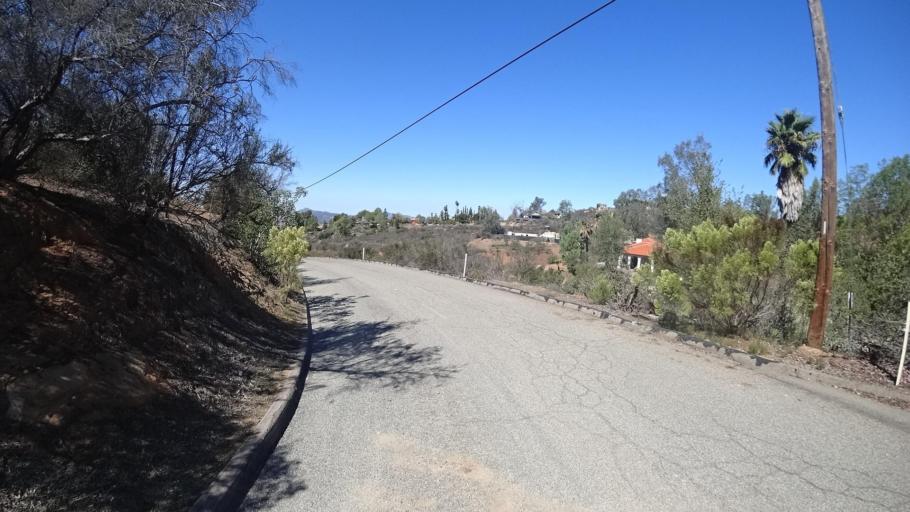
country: US
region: California
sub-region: San Diego County
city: Jamul
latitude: 32.7394
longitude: -116.8712
